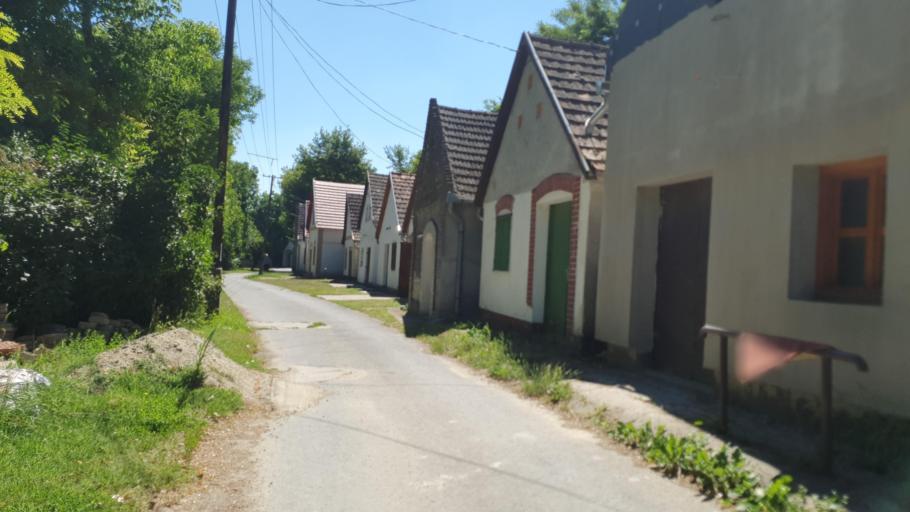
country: HU
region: Bacs-Kiskun
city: Hajos
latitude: 46.3872
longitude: 19.1515
